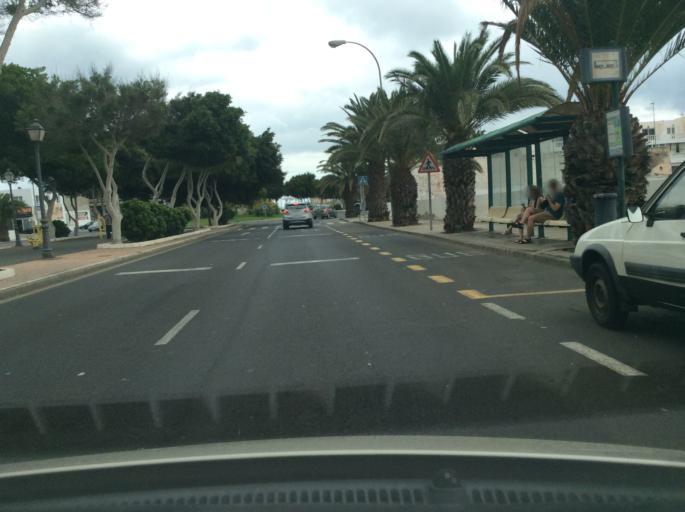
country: ES
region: Canary Islands
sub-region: Provincia de Las Palmas
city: Arrecife
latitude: 28.9682
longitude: -13.5451
